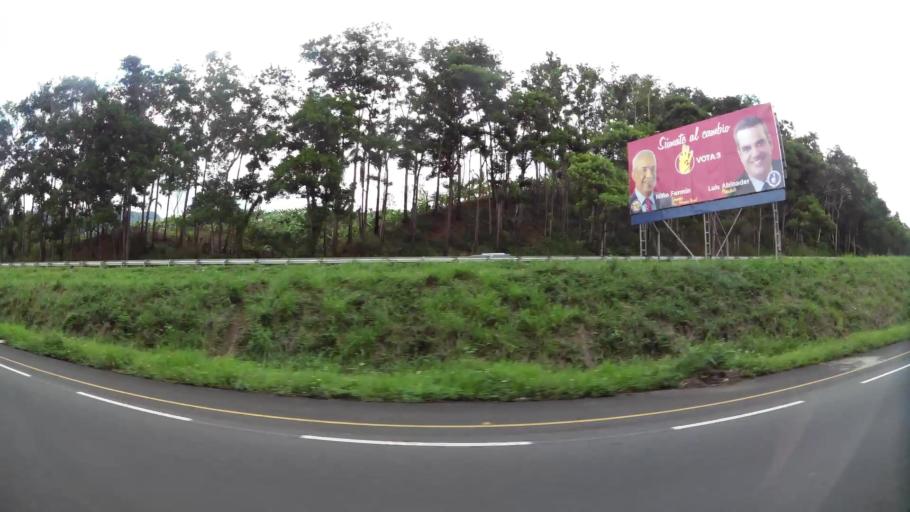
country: DO
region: Monsenor Nouel
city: Piedra Blanca
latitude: 18.8248
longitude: -70.2922
